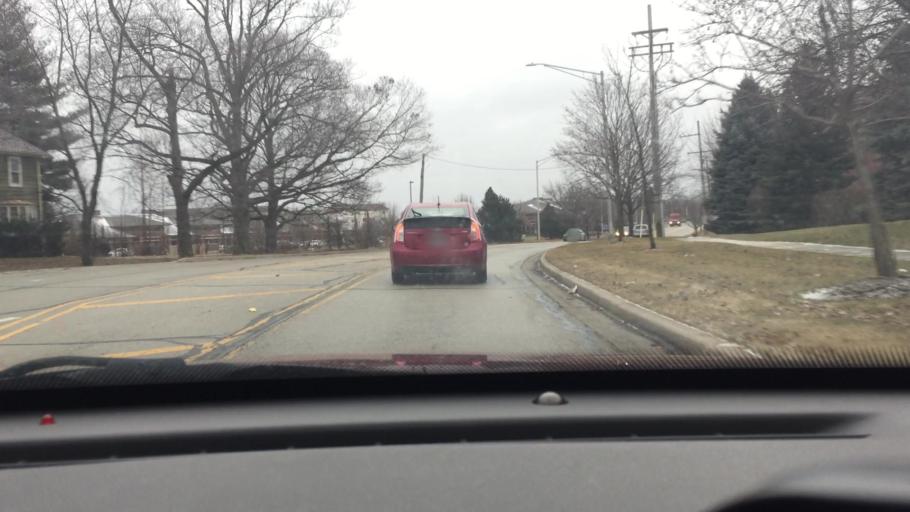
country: US
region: Illinois
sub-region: DuPage County
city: Warrenville
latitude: 41.7843
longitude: -88.1823
